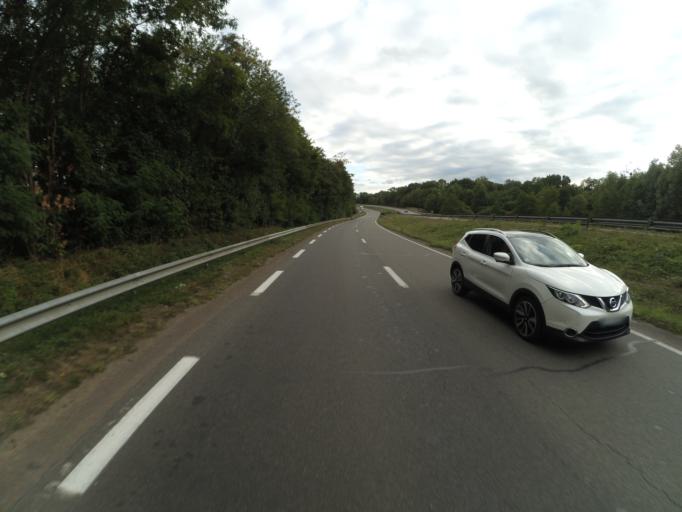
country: FR
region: Pays de la Loire
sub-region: Departement de la Vendee
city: Saligny
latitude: 46.8224
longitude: -1.4289
